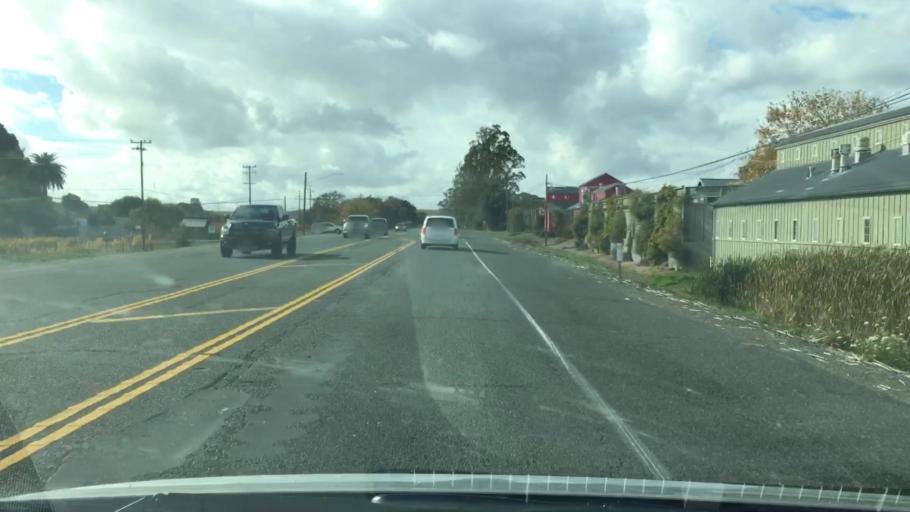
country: US
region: California
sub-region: Napa County
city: Napa
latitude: 38.2554
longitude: -122.3313
